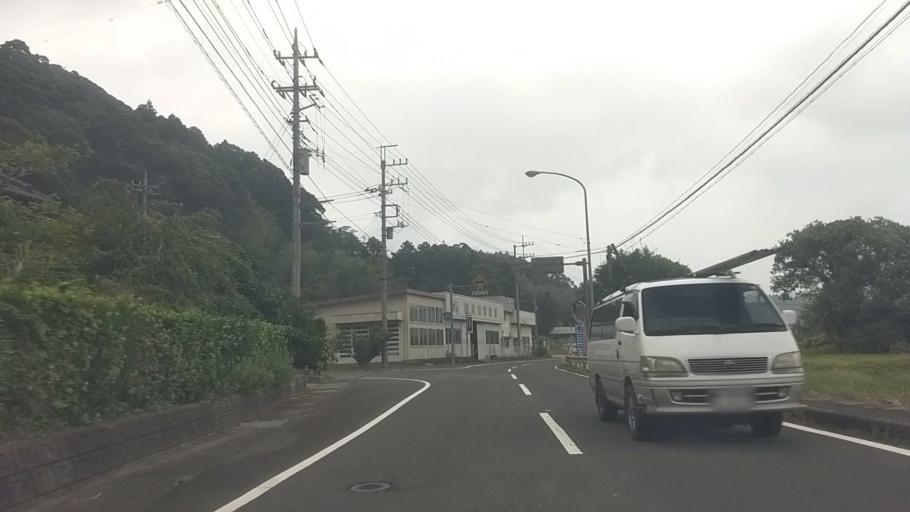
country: JP
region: Chiba
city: Ohara
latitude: 35.2618
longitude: 140.2506
